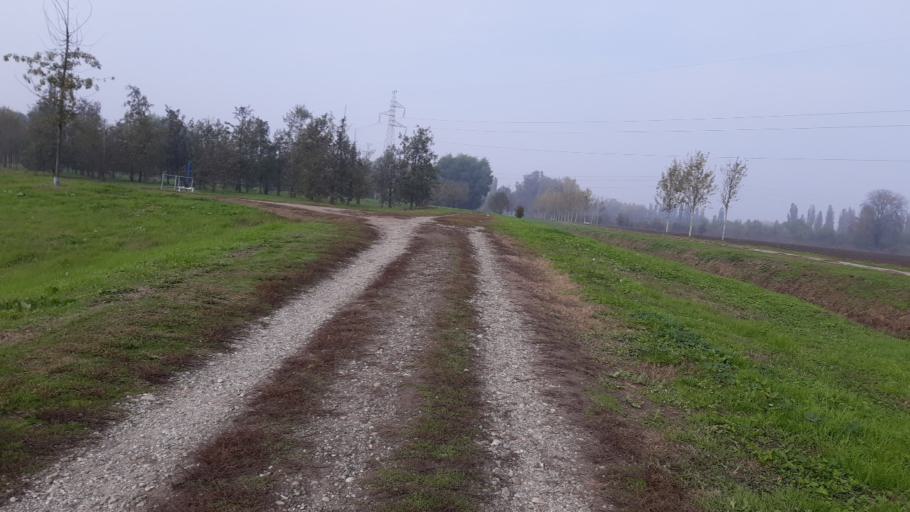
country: IT
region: Lombardy
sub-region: Citta metropolitana di Milano
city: Chiaravalle
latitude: 45.4187
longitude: 9.2276
